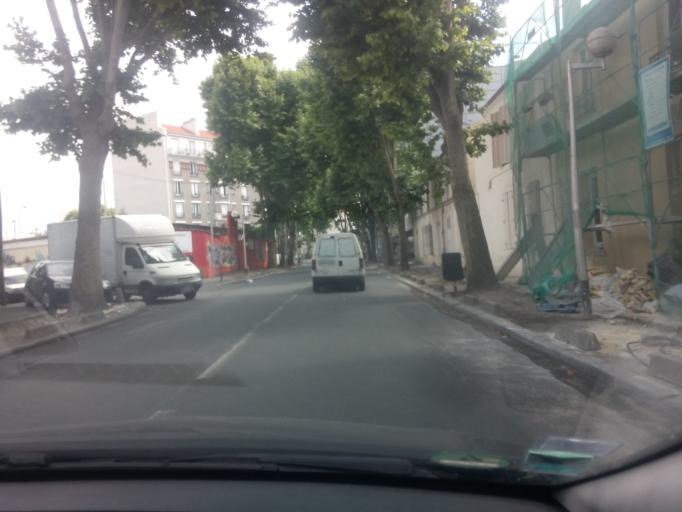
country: FR
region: Ile-de-France
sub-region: Departement de Seine-Saint-Denis
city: Aubervilliers
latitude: 48.9126
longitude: 2.3744
